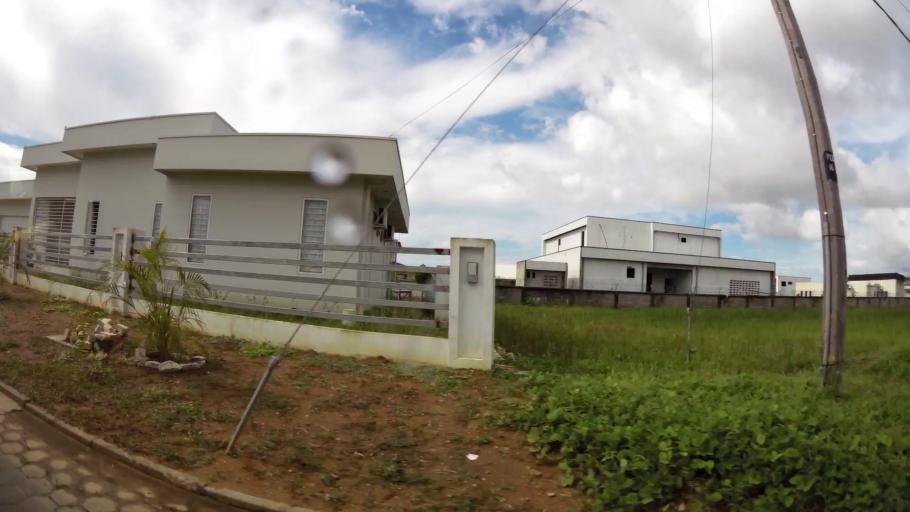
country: SR
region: Paramaribo
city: Paramaribo
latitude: 5.8473
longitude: -55.1924
